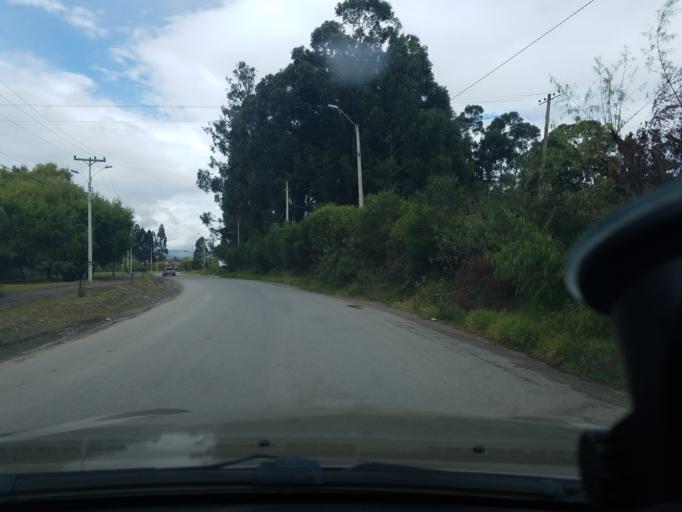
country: EC
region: Azuay
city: Cuenca
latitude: -2.8955
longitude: -78.9670
